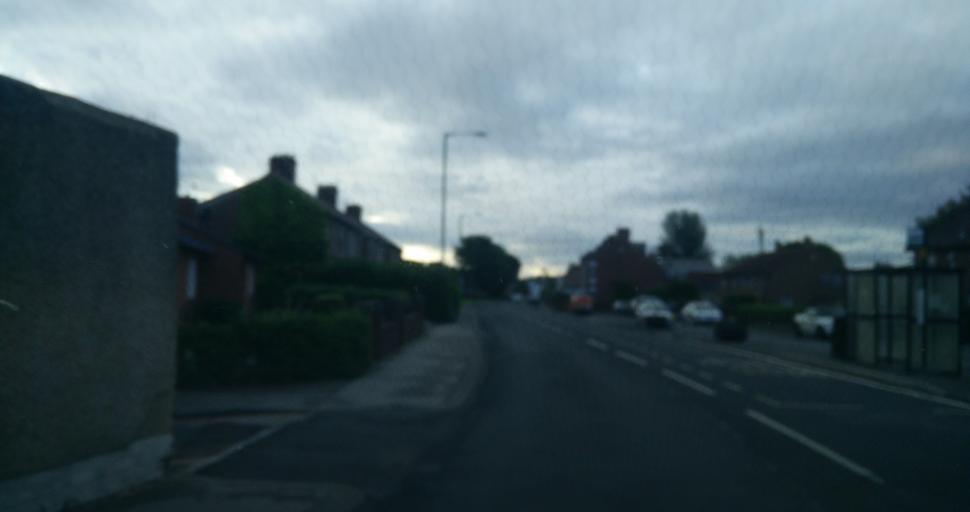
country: GB
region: England
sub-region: County Durham
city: Durham
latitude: 54.7785
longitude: -1.5535
